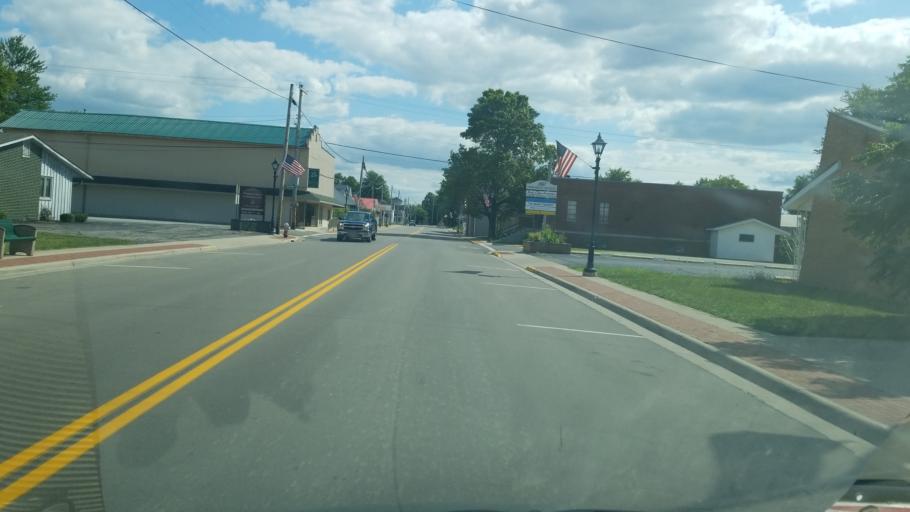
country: US
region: Ohio
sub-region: Logan County
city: Lakeview
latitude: 40.4837
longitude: -83.9241
